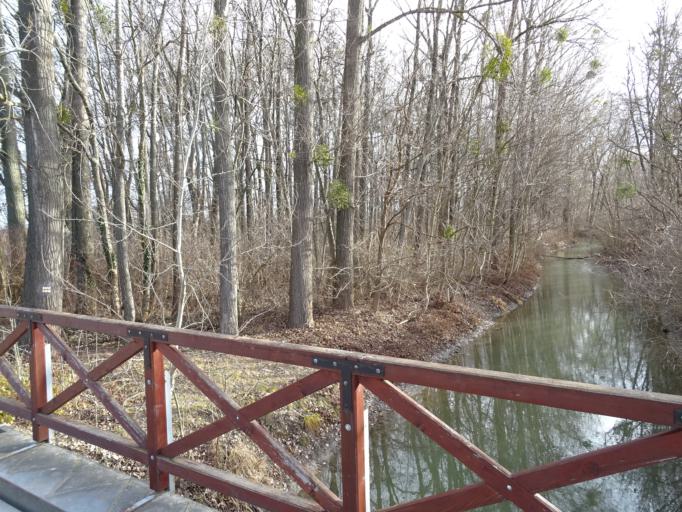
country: HU
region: Gyor-Moson-Sopron
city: Halaszi
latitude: 47.8595
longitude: 17.3473
